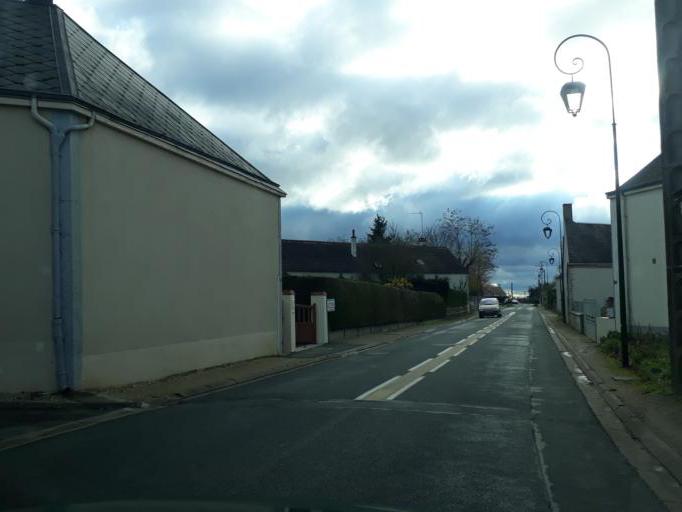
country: FR
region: Centre
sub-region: Departement du Loiret
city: Beaugency
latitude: 47.8002
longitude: 1.5977
